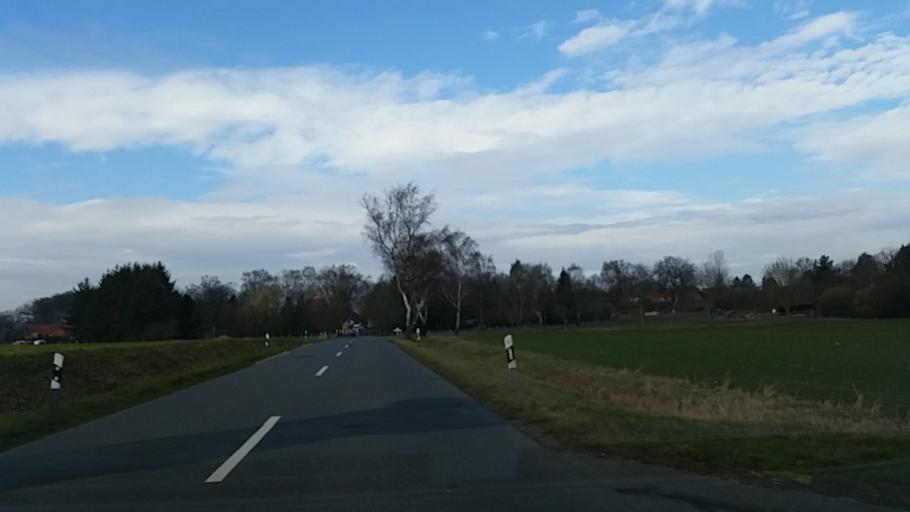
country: DE
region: Lower Saxony
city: Romstedt
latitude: 53.1154
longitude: 10.6433
